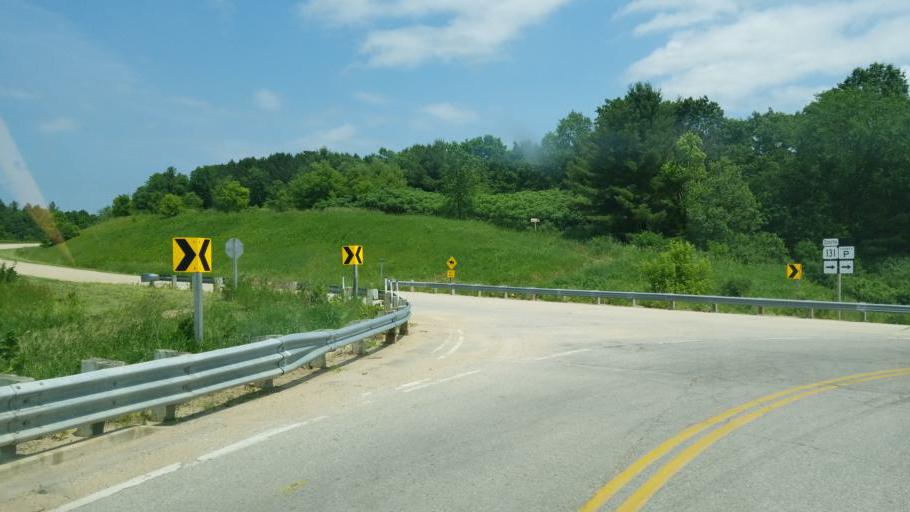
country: US
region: Wisconsin
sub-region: Monroe County
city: Cashton
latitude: 43.6394
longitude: -90.5971
